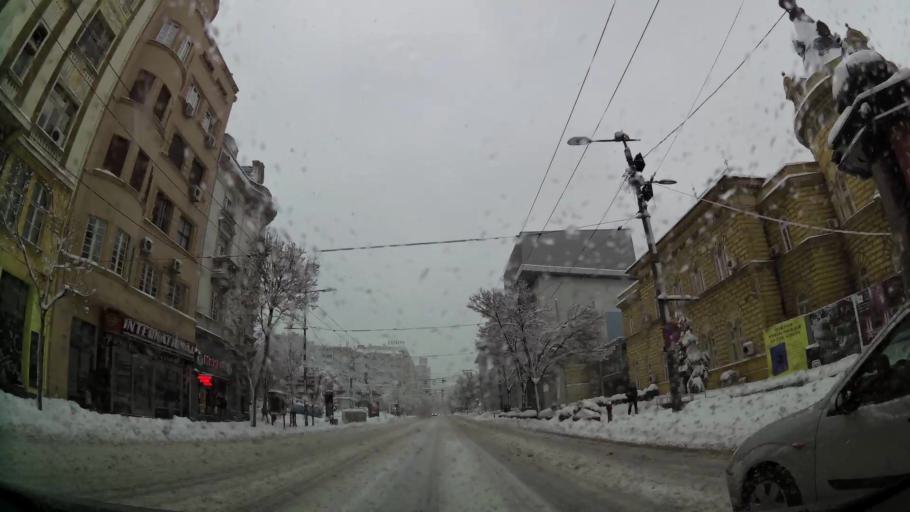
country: RS
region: Central Serbia
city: Belgrade
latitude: 44.8065
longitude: 20.4645
